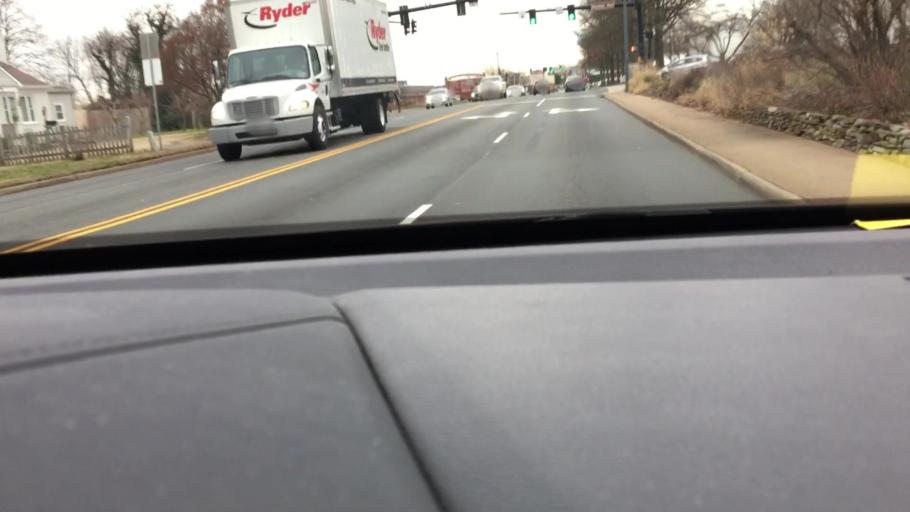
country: US
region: Virginia
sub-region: City of Manassas
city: Manassas
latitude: 38.7572
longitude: -77.4699
